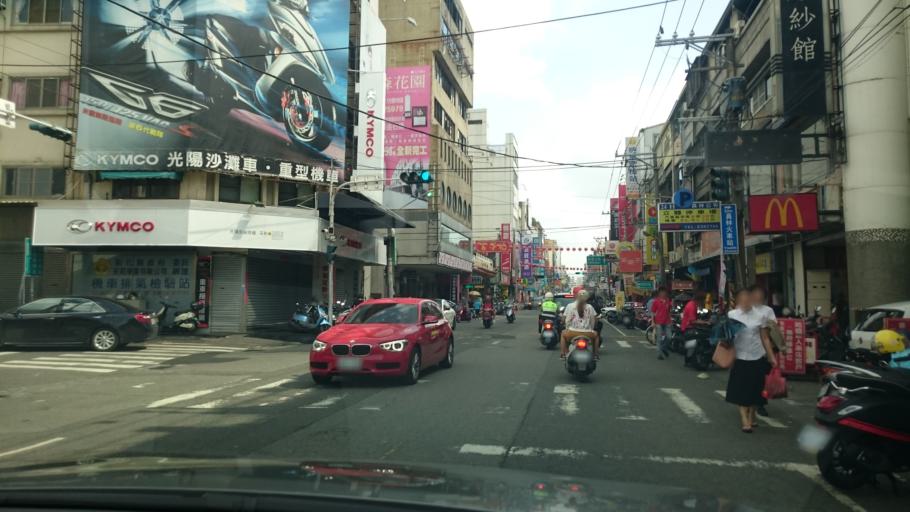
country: TW
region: Taiwan
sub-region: Nantou
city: Nantou
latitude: 23.9607
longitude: 120.5706
